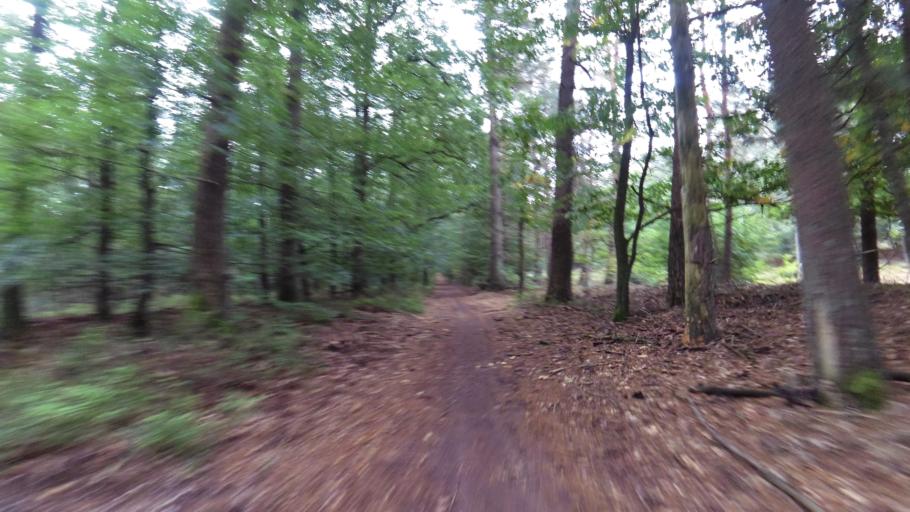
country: NL
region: Gelderland
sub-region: Gemeente Apeldoorn
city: Beekbergen
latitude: 52.1911
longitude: 5.8968
